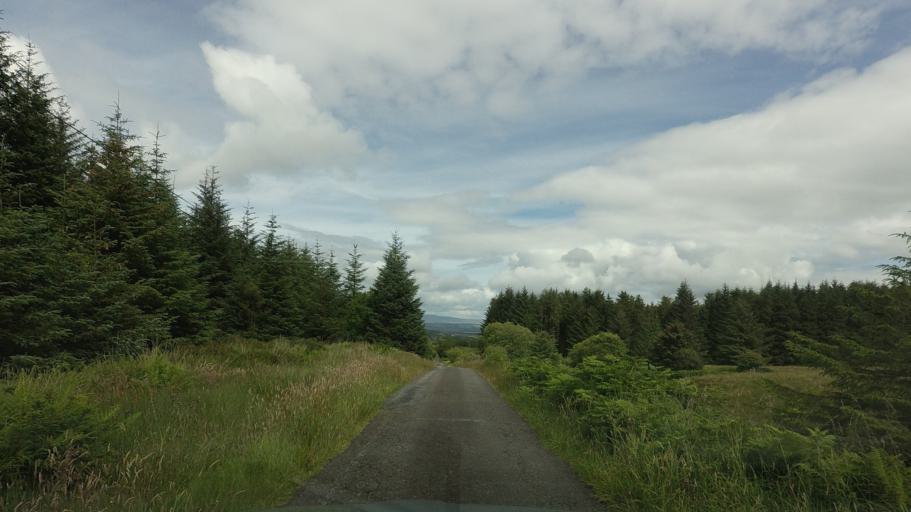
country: GB
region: Scotland
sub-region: Stirling
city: Killearn
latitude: 56.1077
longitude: -4.4109
